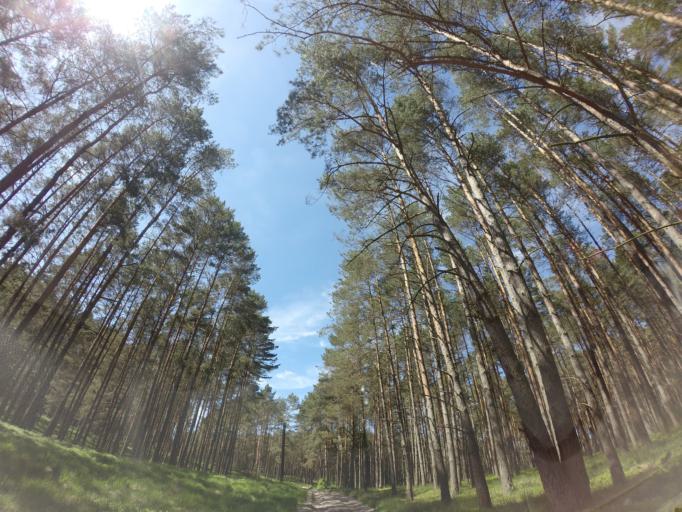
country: PL
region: West Pomeranian Voivodeship
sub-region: Powiat choszczenski
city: Drawno
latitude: 53.1274
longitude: 15.7933
